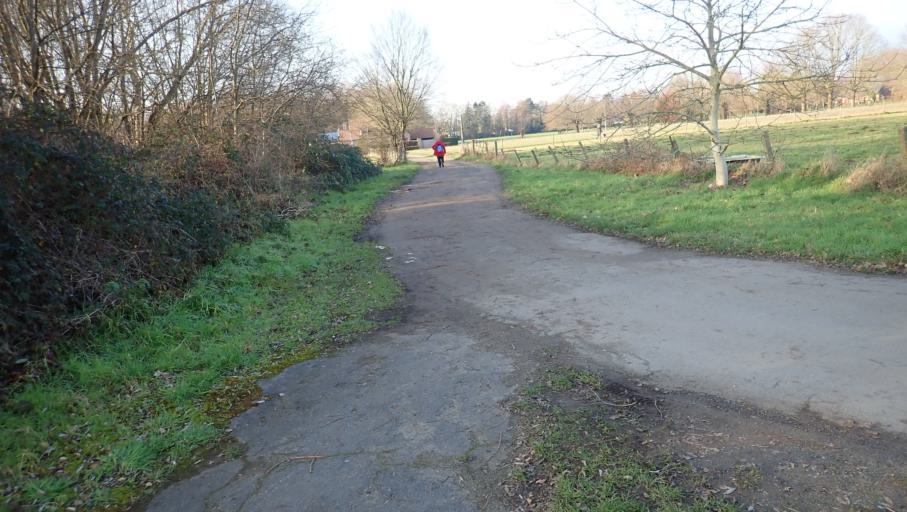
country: BE
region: Flanders
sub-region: Provincie Vlaams-Brabant
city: Tremelo
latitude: 51.0090
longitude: 4.7075
